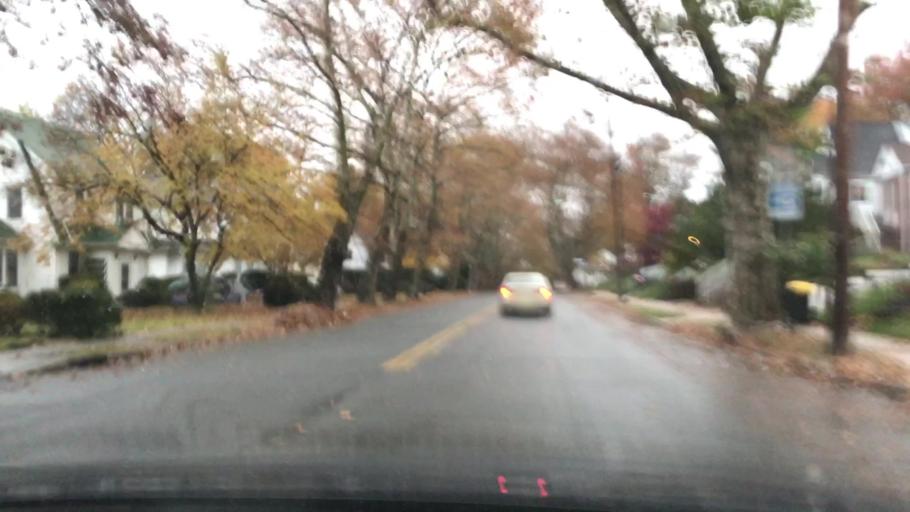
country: US
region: New Jersey
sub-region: Bergen County
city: Bogota
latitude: 40.8819
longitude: -74.0226
